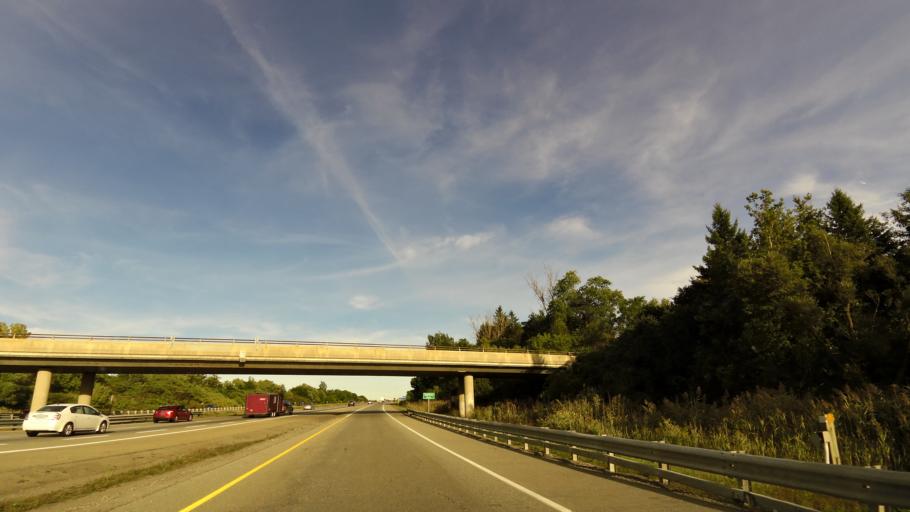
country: CA
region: Ontario
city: Ancaster
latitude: 43.2045
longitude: -80.0019
